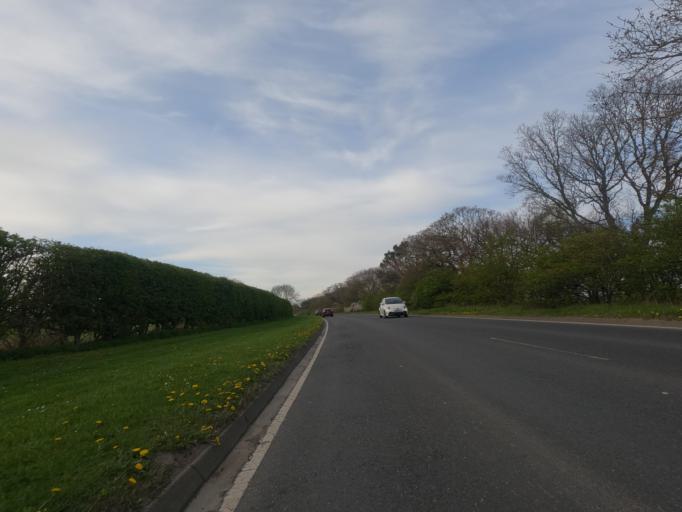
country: GB
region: England
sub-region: Newcastle upon Tyne
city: Dinnington
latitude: 55.0352
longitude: -1.6651
